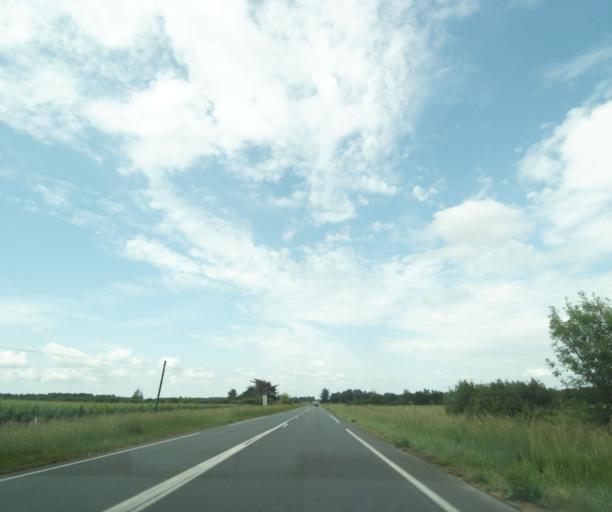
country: FR
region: Pays de la Loire
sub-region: Departement de Maine-et-Loire
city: Montreuil-Bellay
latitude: 47.1448
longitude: -0.1521
